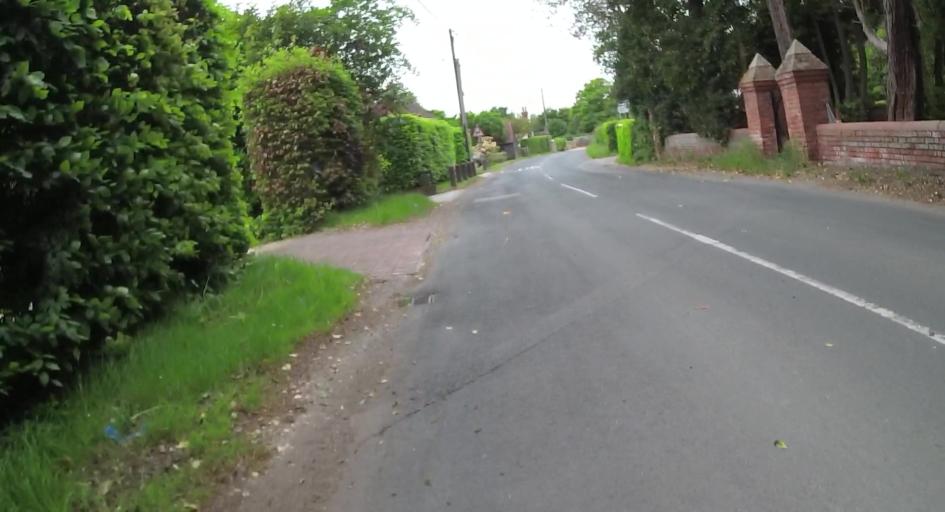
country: GB
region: England
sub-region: West Berkshire
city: Arborfield
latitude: 51.3738
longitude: -0.9226
